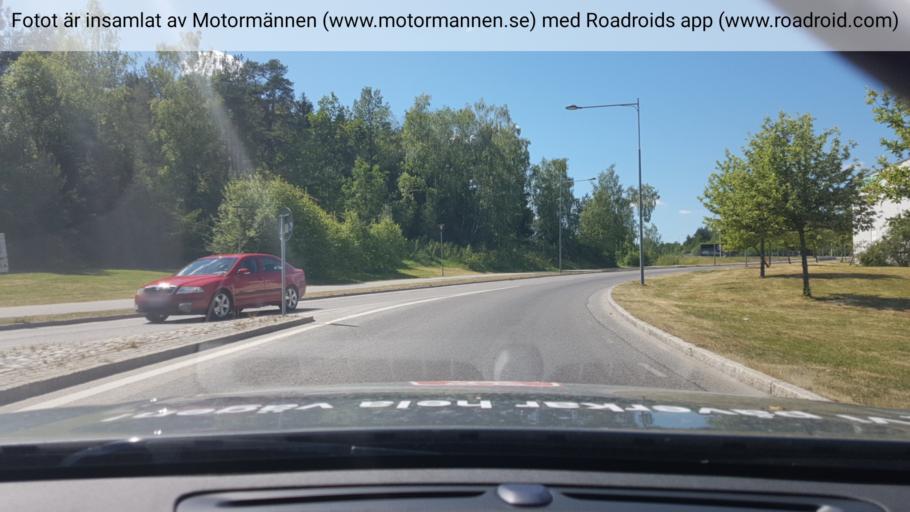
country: SE
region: Stockholm
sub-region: Jarfalla Kommun
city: Jakobsberg
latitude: 59.3877
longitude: 17.8801
